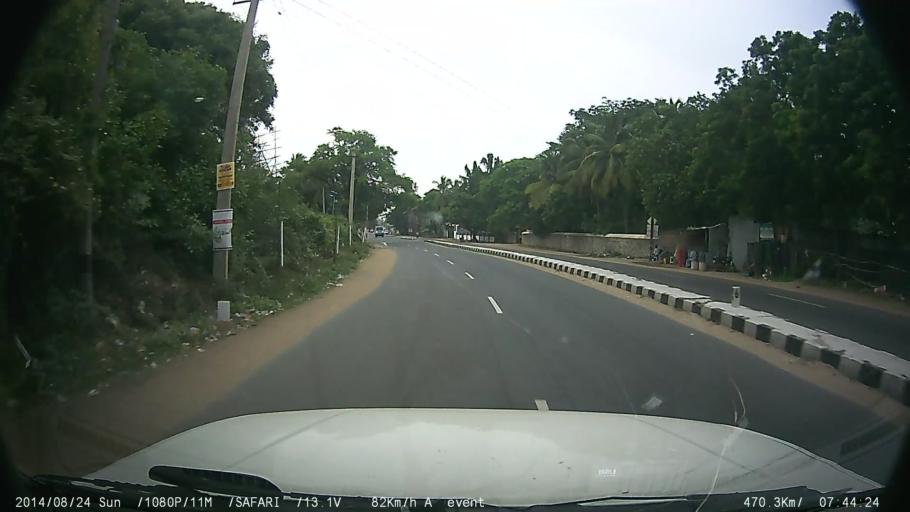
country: IN
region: Tamil Nadu
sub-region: Kancheepuram
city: Injambakkam
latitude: 12.8264
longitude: 80.2313
